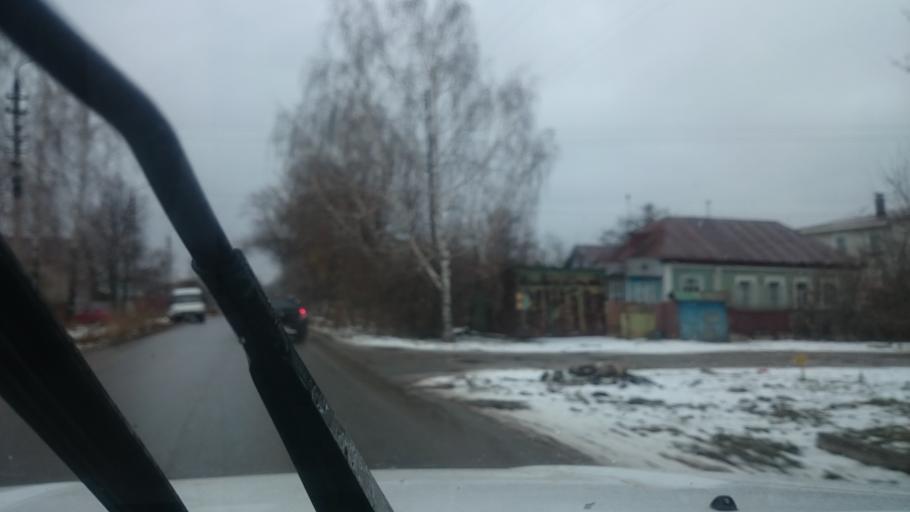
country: RU
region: Tula
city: Tula
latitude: 54.2036
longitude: 37.5580
